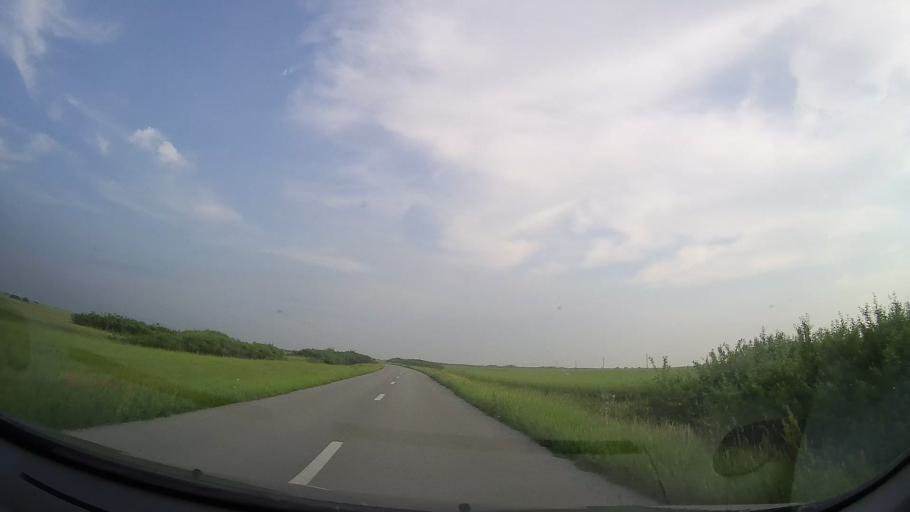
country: RS
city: Jasa Tomic
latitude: 45.4788
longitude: 20.8462
